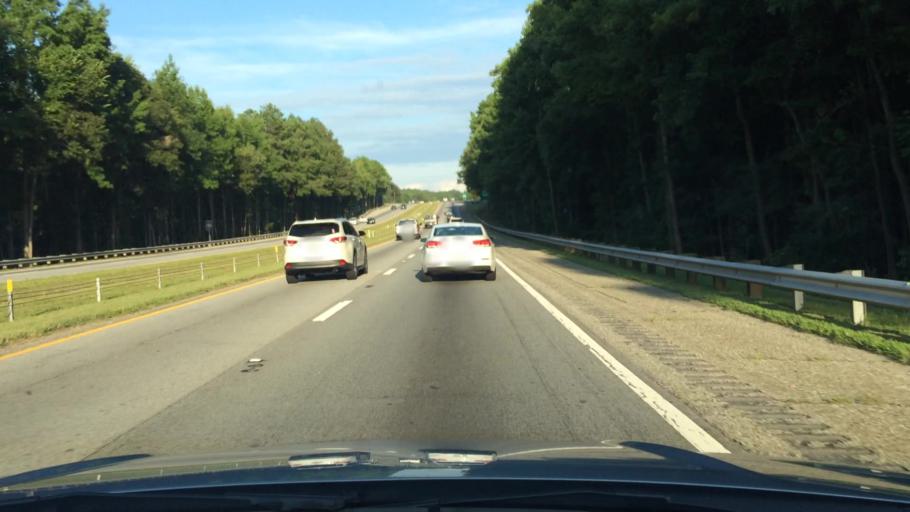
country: US
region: South Carolina
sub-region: Lexington County
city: Chapin
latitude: 34.2228
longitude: -81.4184
